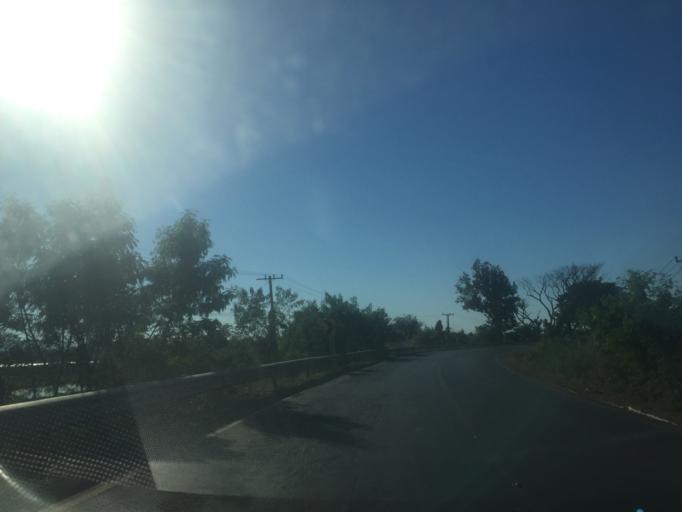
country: TH
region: Kalasin
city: Tha Khantho
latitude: 16.9619
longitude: 103.2561
